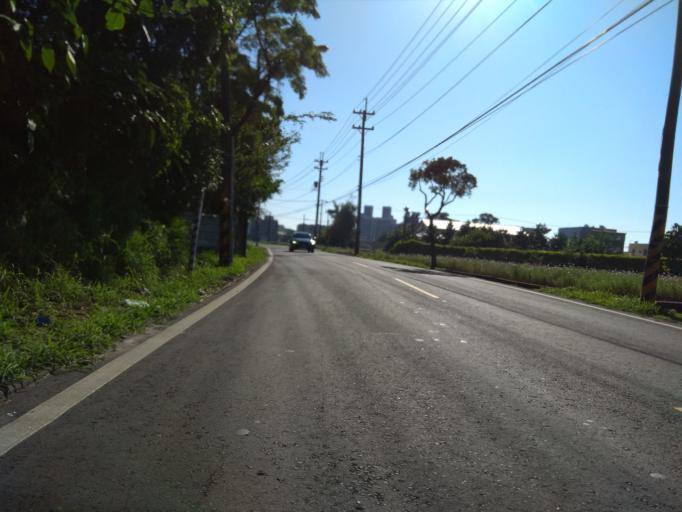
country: TW
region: Taiwan
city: Taoyuan City
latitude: 24.9903
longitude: 121.1937
